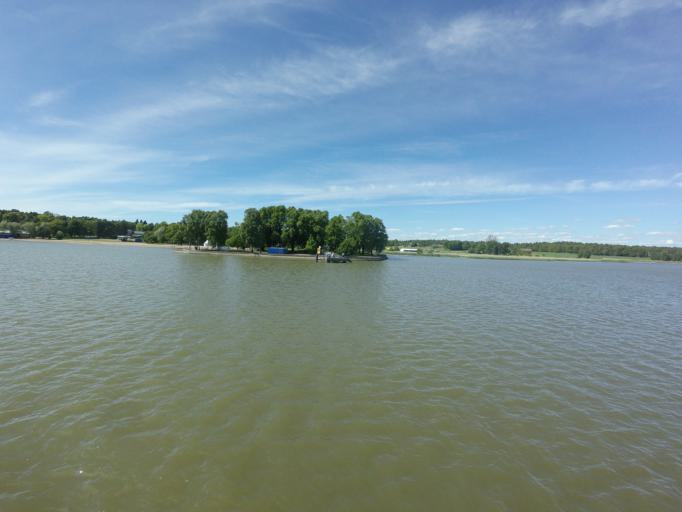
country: FI
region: Varsinais-Suomi
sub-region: Turku
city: Raisio
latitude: 60.4259
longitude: 22.1872
